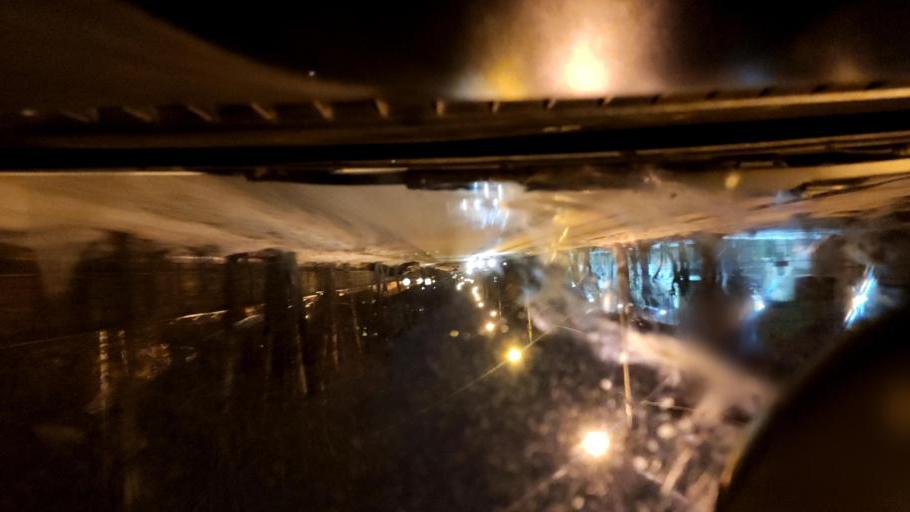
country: RU
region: Perm
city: Kultayevo
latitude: 57.9915
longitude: 55.9402
